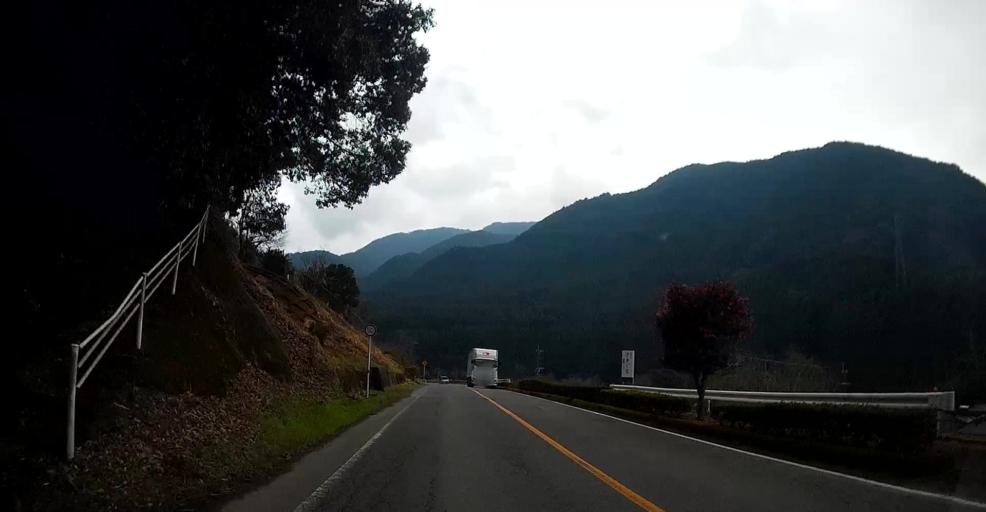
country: JP
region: Kumamoto
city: Matsubase
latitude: 32.6146
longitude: 130.8441
